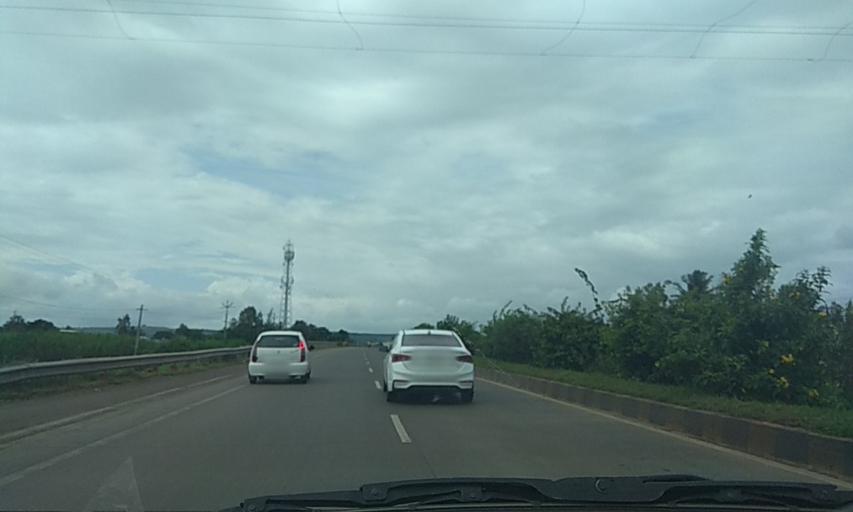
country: IN
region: Maharashtra
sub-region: Kolhapur
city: Kagal
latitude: 16.5659
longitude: 74.3155
